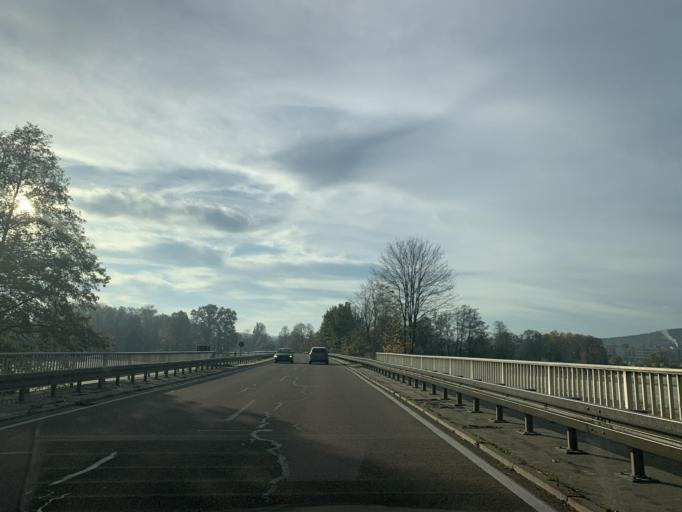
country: DE
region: Bavaria
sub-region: Upper Palatinate
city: Neunburg vorm Wald
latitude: 49.3562
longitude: 12.3752
